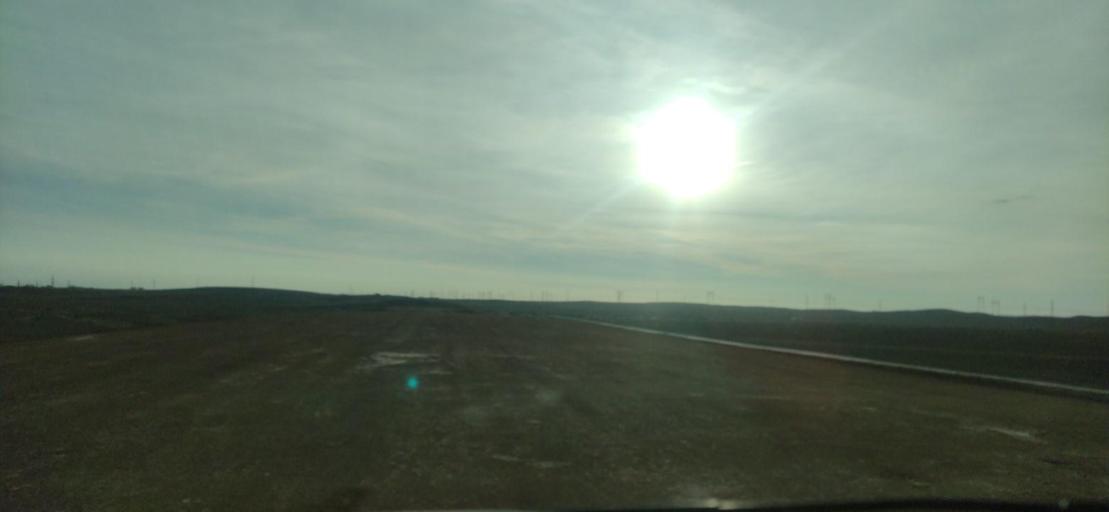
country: KZ
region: Qaraghandy
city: Saryshaghan
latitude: 46.1358
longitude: 73.6033
